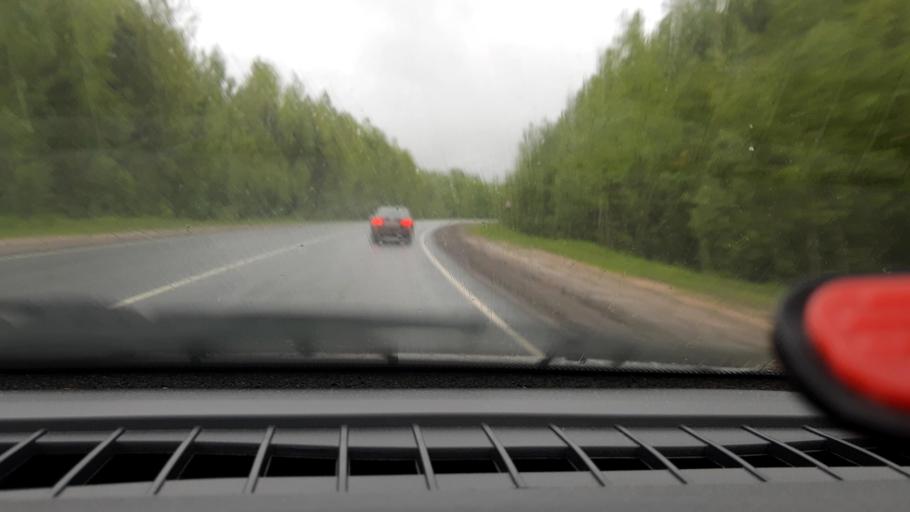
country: RU
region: Nizjnij Novgorod
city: Semenov
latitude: 56.7561
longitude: 44.3640
